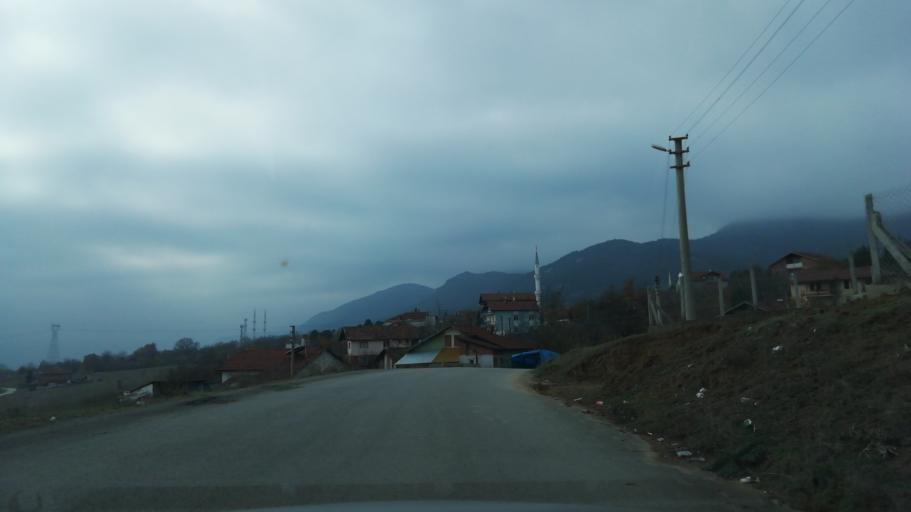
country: TR
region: Karabuk
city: Karabuk
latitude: 41.2319
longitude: 32.6281
